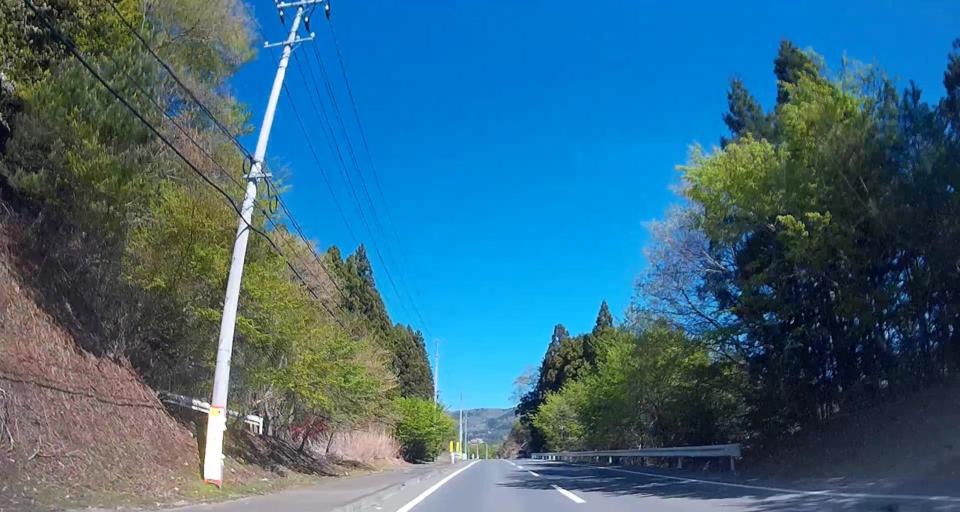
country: JP
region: Miyagi
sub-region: Oshika Gun
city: Onagawa Cho
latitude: 38.5081
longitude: 141.4859
